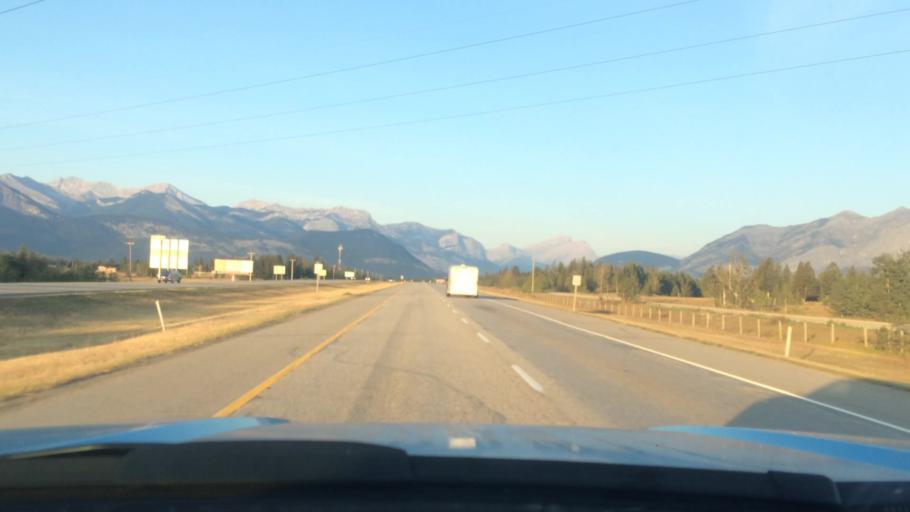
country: CA
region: Alberta
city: Canmore
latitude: 51.0994
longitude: -115.0323
